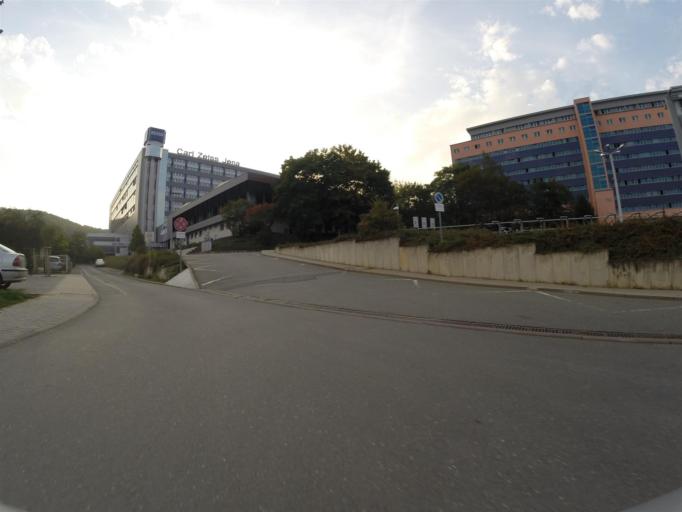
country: DE
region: Thuringia
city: Jena
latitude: 50.9163
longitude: 11.5681
